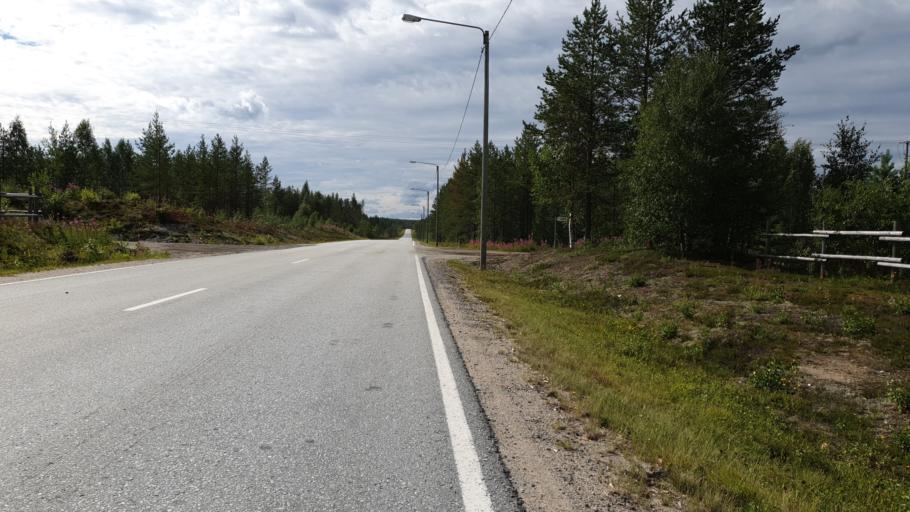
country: FI
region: Kainuu
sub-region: Kehys-Kainuu
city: Kuhmo
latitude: 64.5323
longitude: 29.9444
